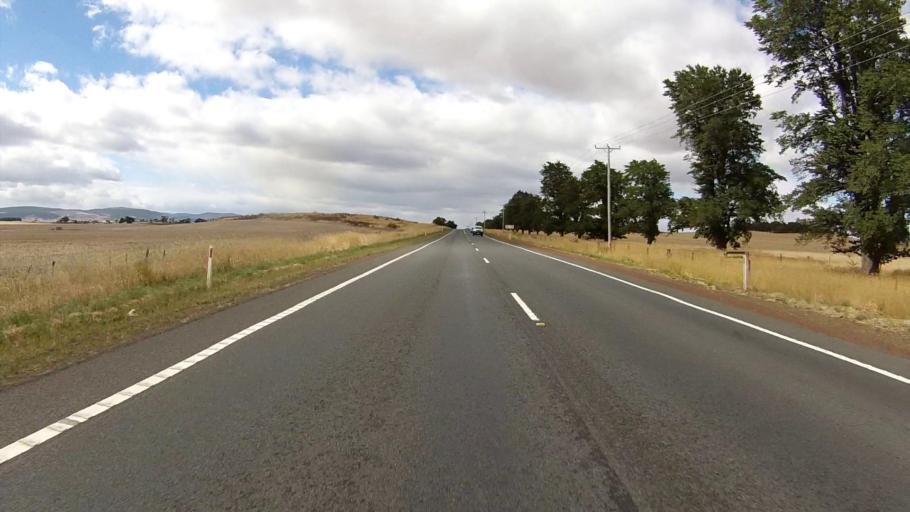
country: AU
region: Tasmania
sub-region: Northern Midlands
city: Evandale
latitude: -41.9023
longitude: 147.4769
